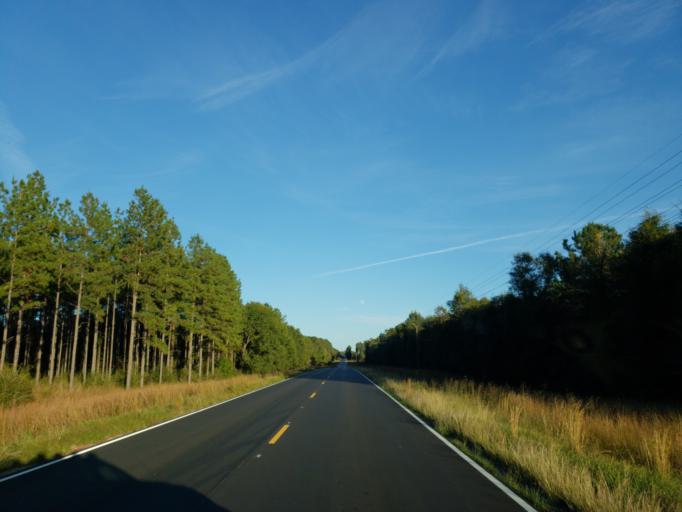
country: US
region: Mississippi
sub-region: Wayne County
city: Belmont
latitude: 31.4216
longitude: -88.5320
